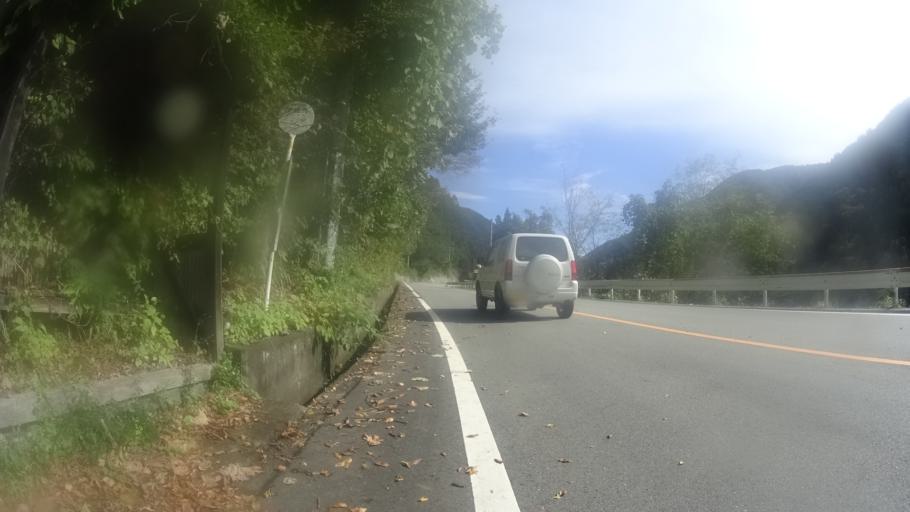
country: JP
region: Yamanashi
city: Otsuki
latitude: 35.7880
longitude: 138.9280
